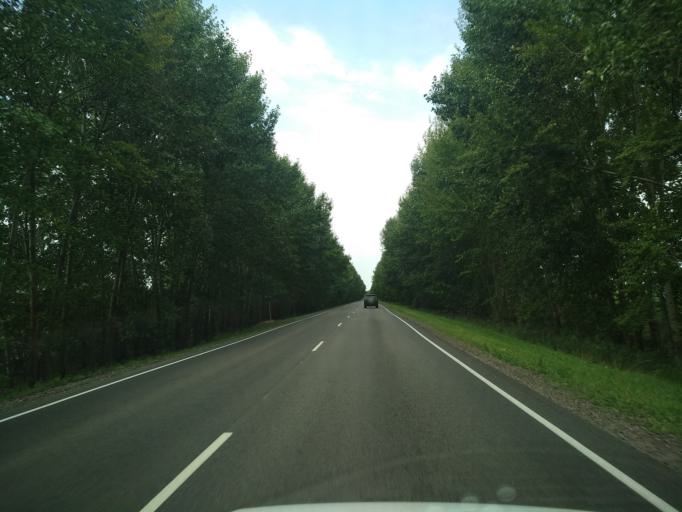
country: RU
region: Voronezj
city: Pereleshino
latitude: 51.8022
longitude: 40.1766
